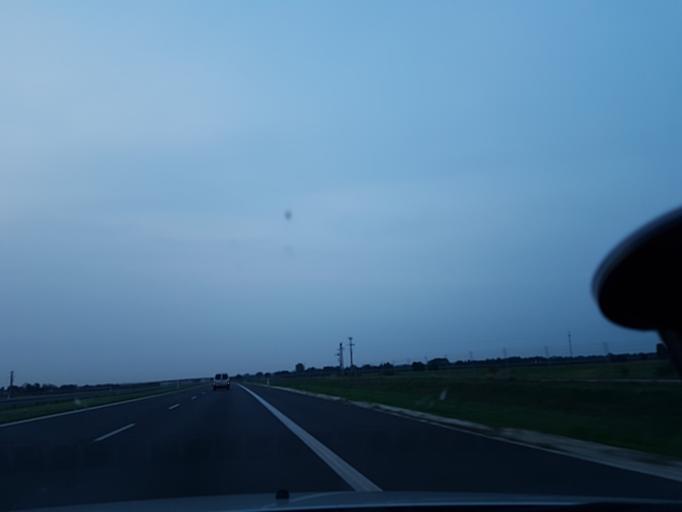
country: PL
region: Lodz Voivodeship
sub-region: Powiat zgierski
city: Strykow
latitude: 51.9853
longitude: 19.5567
